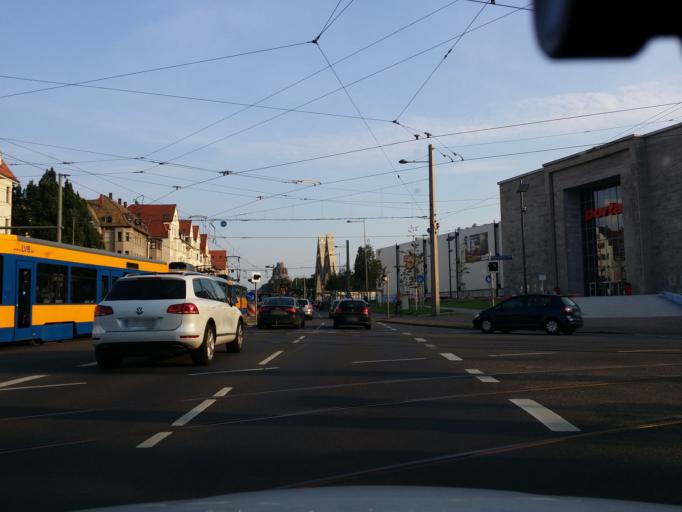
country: DE
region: Saxony
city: Leipzig
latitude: 51.3218
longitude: 12.4035
